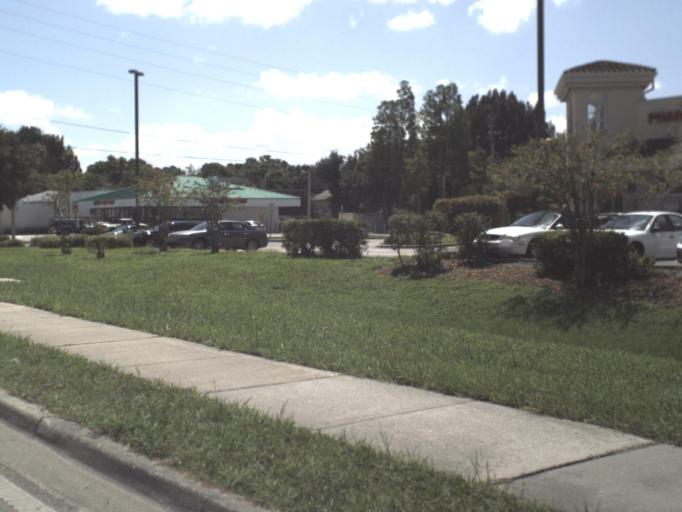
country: US
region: Florida
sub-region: Pinellas County
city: South Highpoint
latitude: 27.9161
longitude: -82.7143
